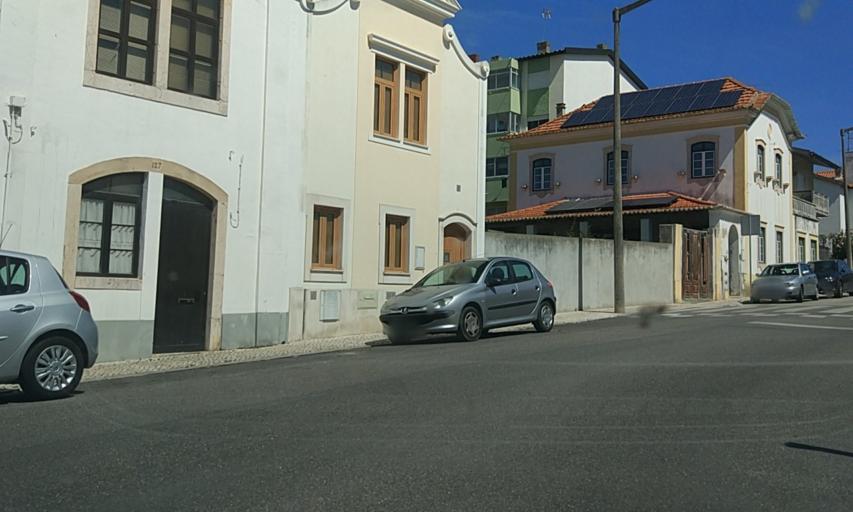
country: PT
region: Coimbra
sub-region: Figueira da Foz
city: Figueira da Foz
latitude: 40.1524
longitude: -8.8530
